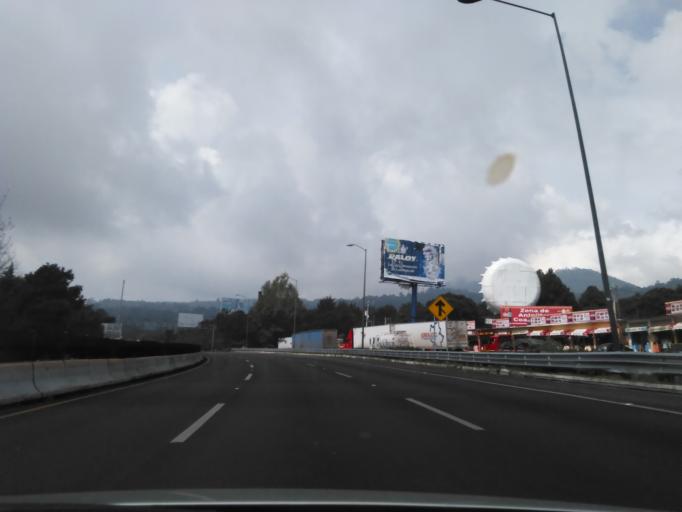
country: MX
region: Morelos
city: Tres Marias
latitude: 19.0297
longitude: -99.1994
